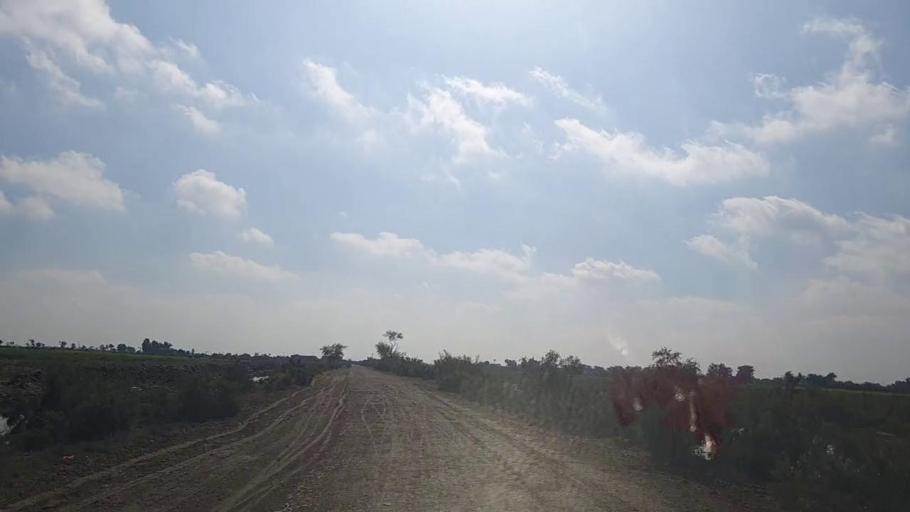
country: PK
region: Sindh
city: Sanghar
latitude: 26.0522
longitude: 69.0045
